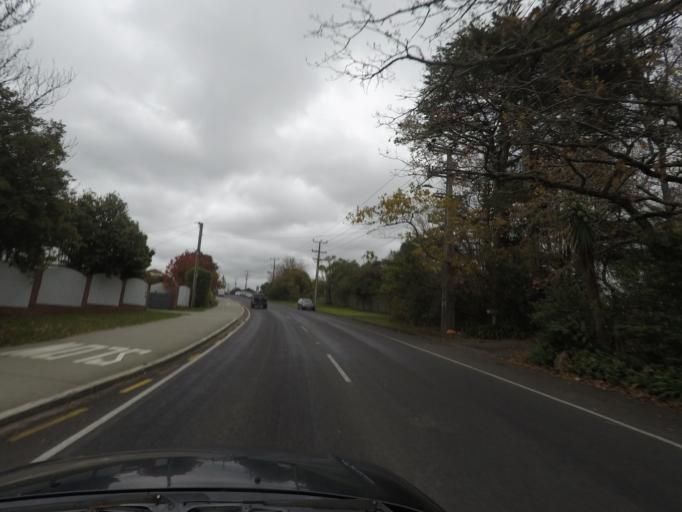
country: NZ
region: Auckland
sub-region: Auckland
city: Waitakere
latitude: -36.9103
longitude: 174.6229
